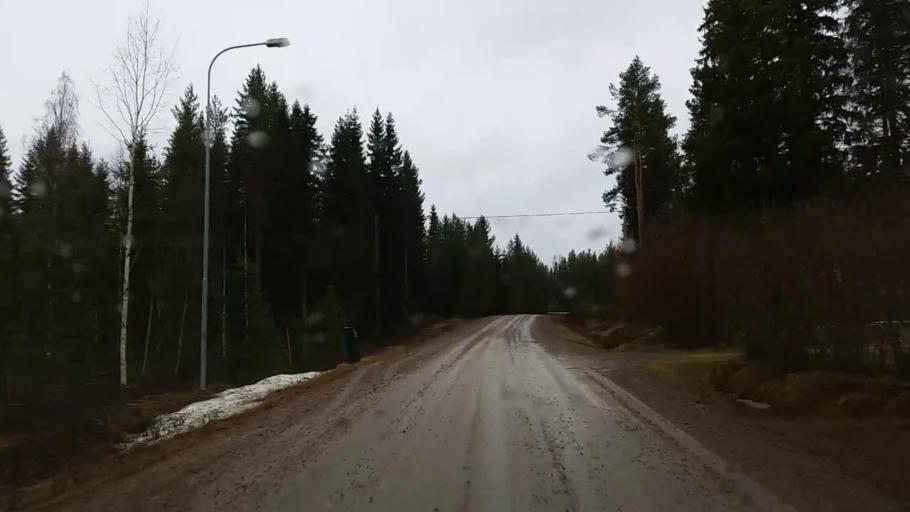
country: SE
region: Vaesternorrland
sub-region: Ange Kommun
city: Ange
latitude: 62.1406
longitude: 15.6606
